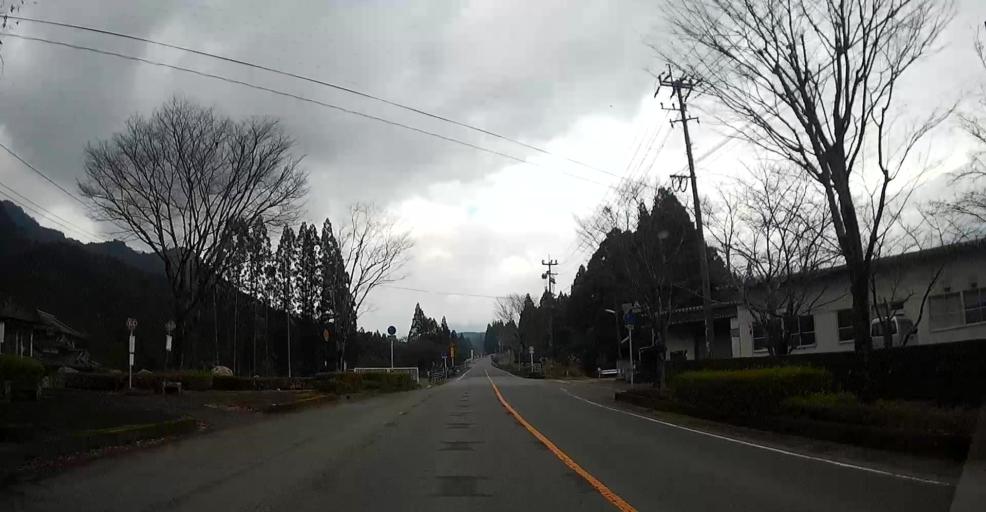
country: JP
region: Kumamoto
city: Matsubase
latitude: 32.6223
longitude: 130.8285
